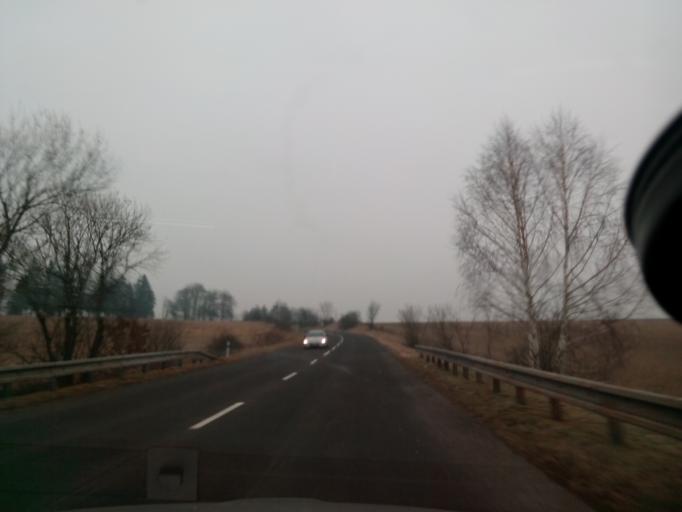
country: SK
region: Kosicky
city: Moldava nad Bodvou
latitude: 48.6824
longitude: 21.0720
